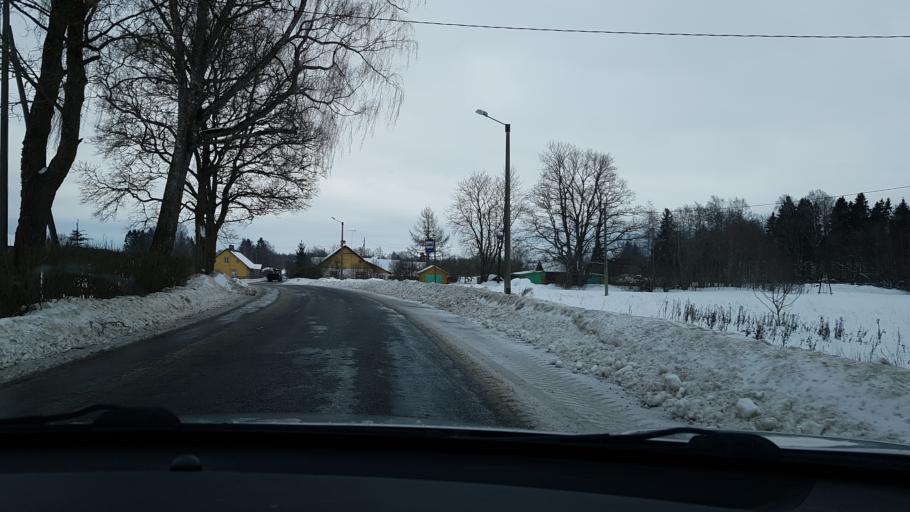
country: EE
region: Jaervamaa
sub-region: Koeru vald
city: Koeru
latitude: 58.9732
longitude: 26.0068
